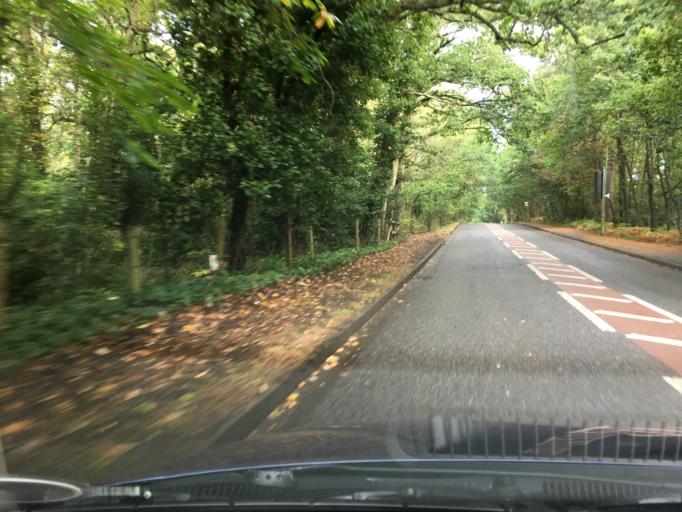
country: GB
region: England
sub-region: Bracknell Forest
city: Crowthorne
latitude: 51.3795
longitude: -0.8053
